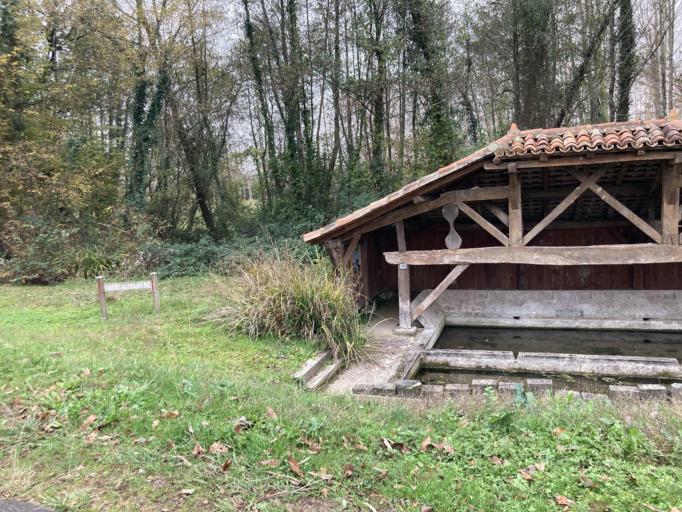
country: FR
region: Aquitaine
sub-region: Departement des Landes
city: Hinx
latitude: 43.7468
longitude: -0.9069
